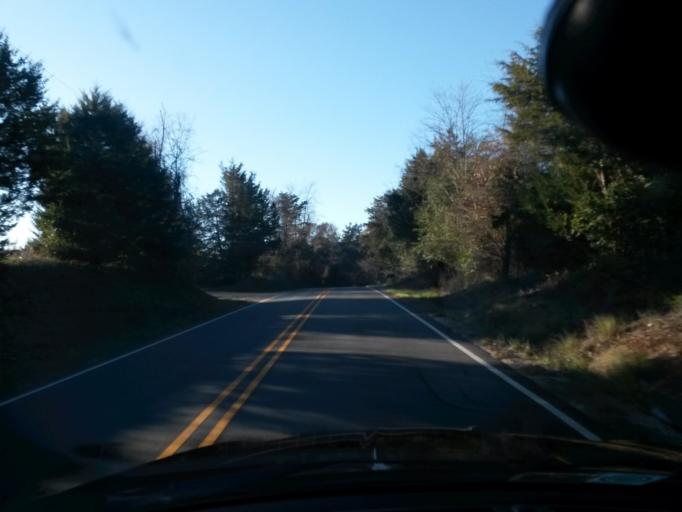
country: US
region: Virginia
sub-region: Amherst County
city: Amherst
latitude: 37.6035
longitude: -79.0700
